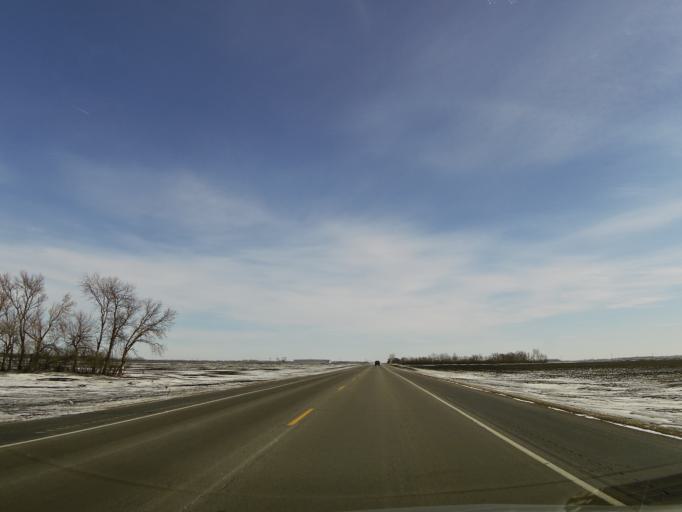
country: US
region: North Dakota
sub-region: Walsh County
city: Grafton
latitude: 48.4123
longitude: -97.3553
